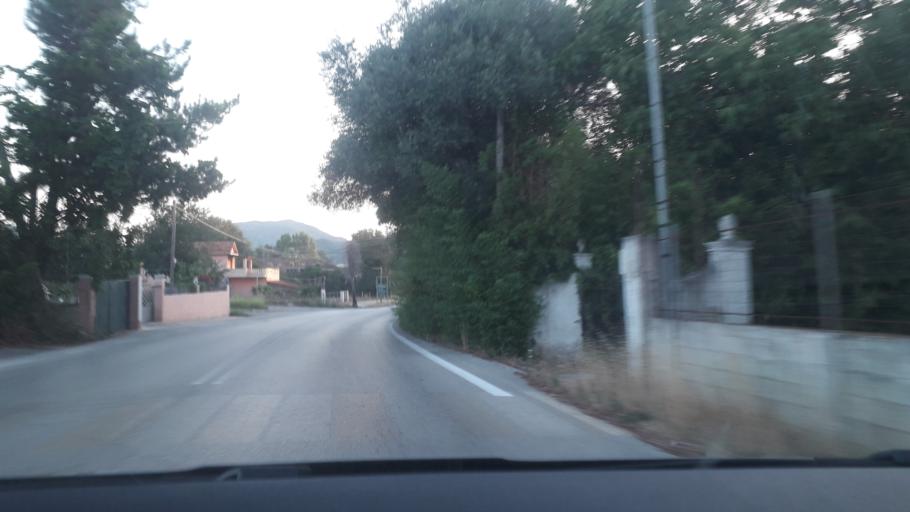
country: GR
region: Ionian Islands
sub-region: Nomos Kerkyras
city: Agios Matthaios
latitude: 39.4724
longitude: 19.9114
